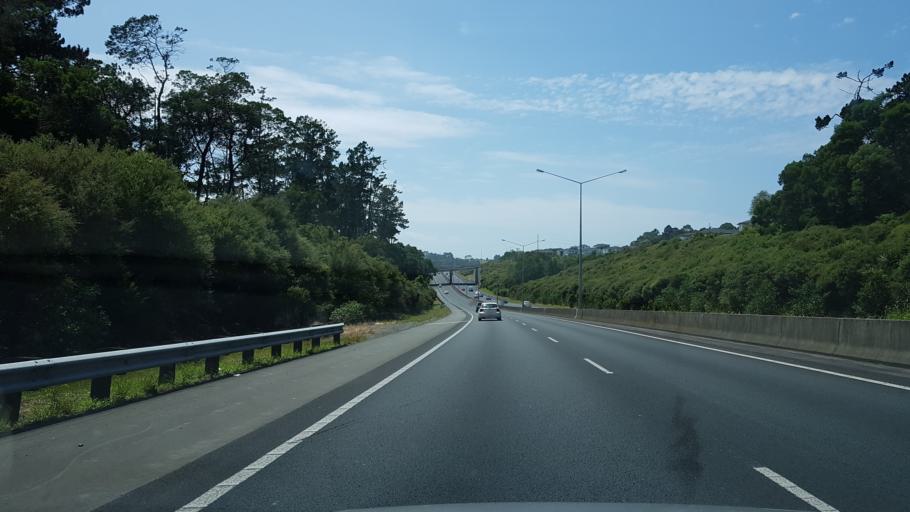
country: NZ
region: Auckland
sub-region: Auckland
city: North Shore
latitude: -36.7755
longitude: 174.6836
